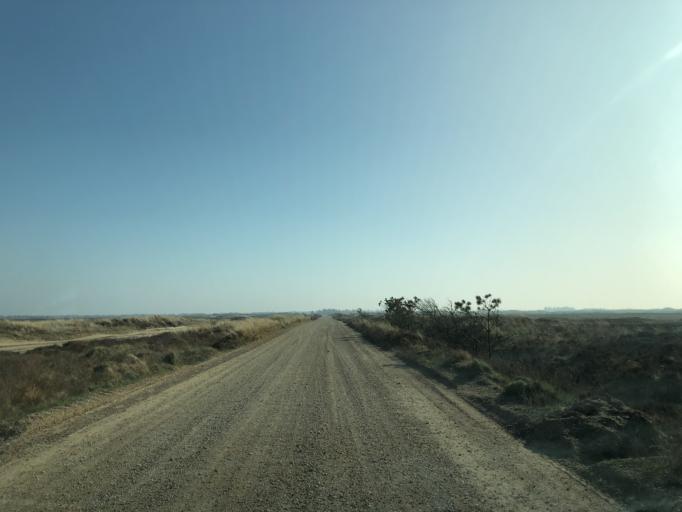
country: DK
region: South Denmark
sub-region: Varde Kommune
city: Oksbol
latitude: 55.5804
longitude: 8.1434
